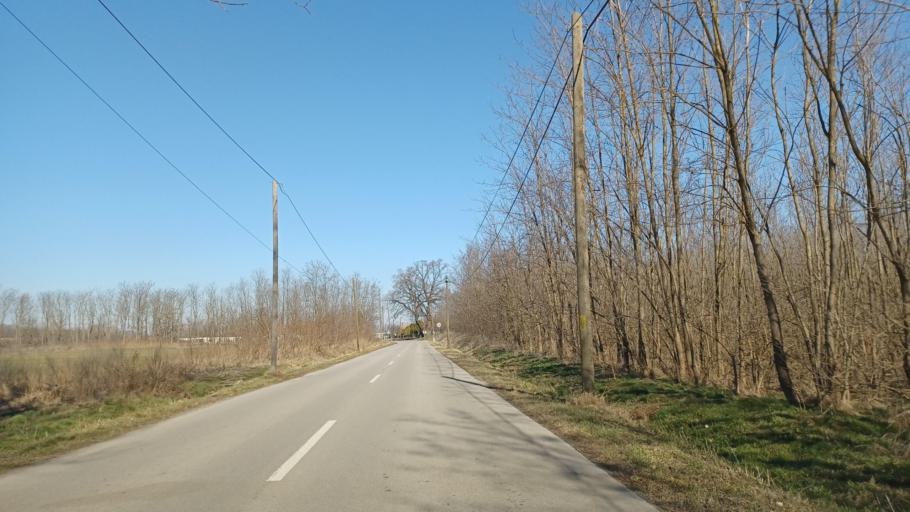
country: HU
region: Tolna
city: Tengelic
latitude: 46.5425
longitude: 18.7026
